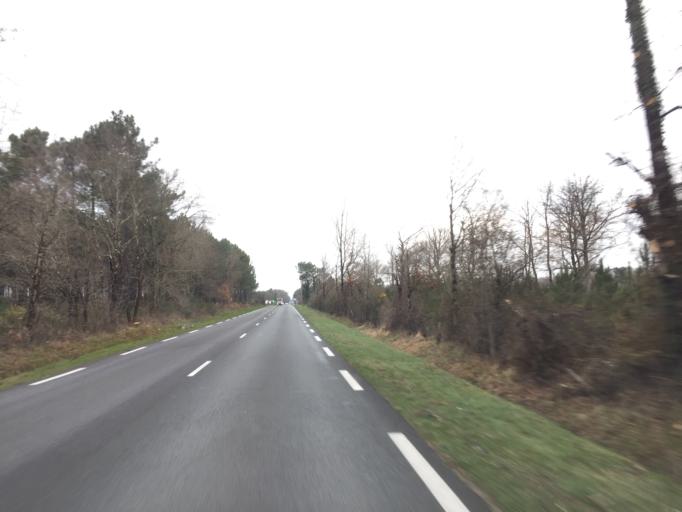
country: FR
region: Aquitaine
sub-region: Departement de la Gironde
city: Saint-Sauveur
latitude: 45.1803
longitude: -0.8432
